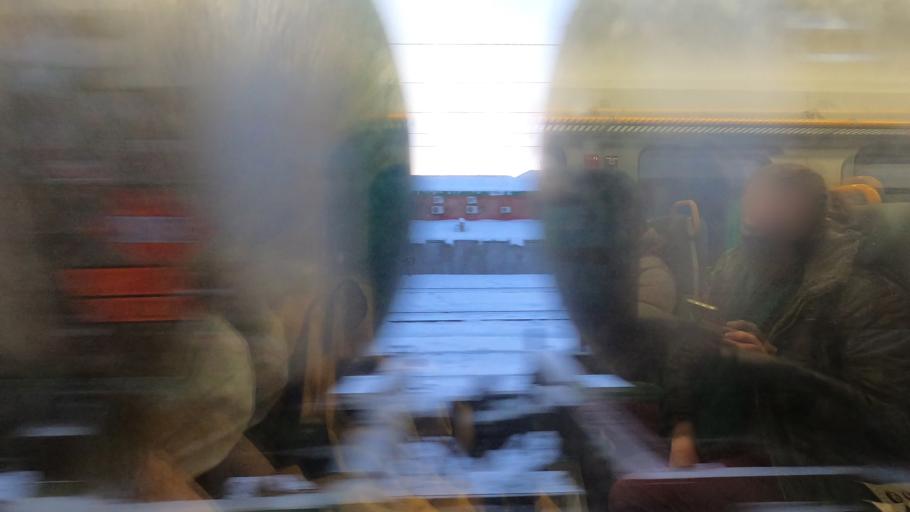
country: RU
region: Moskovskaya
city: Lobnya
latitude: 56.0134
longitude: 37.4847
